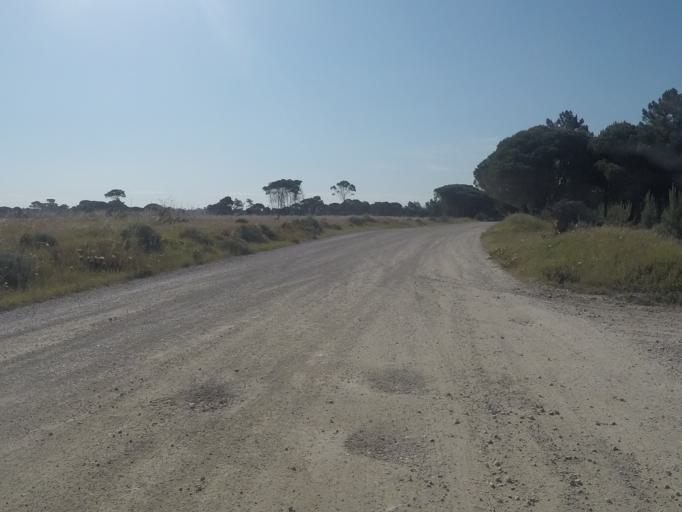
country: PT
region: Setubal
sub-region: Sesimbra
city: Sesimbra
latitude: 38.4919
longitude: -9.1773
